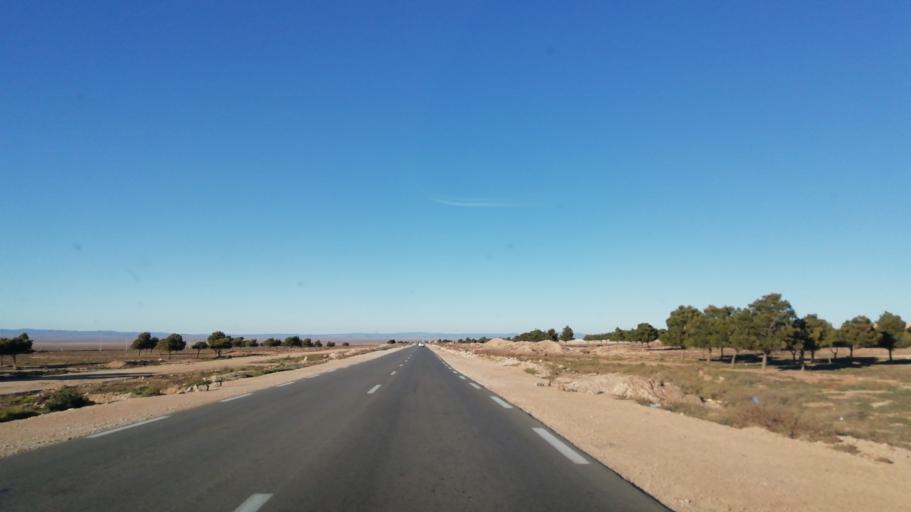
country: DZ
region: Tlemcen
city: Sebdou
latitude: 34.2931
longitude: -1.2603
